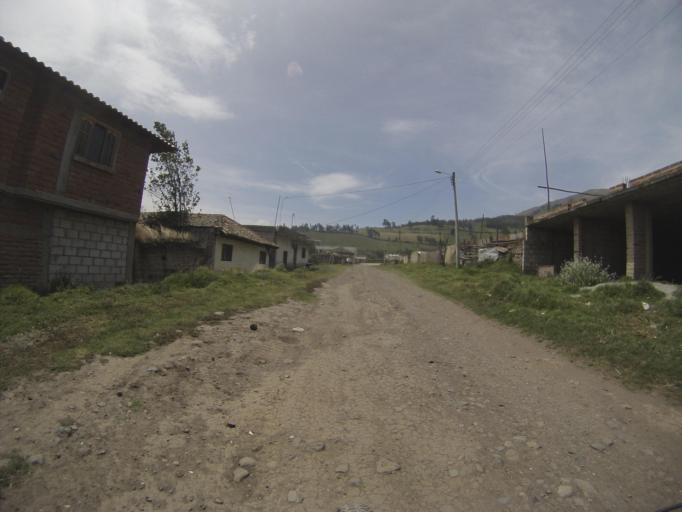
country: EC
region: Pichincha
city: Cayambe
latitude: 0.1553
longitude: -78.0693
